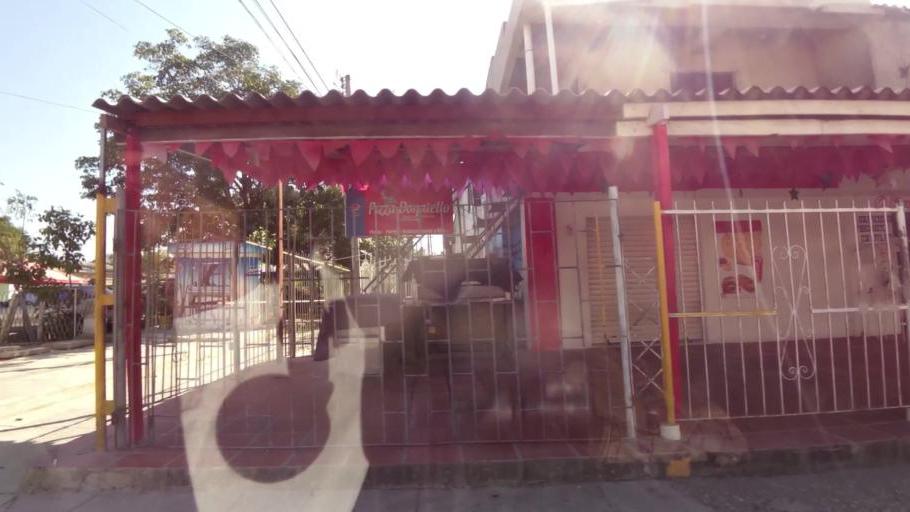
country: CO
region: Bolivar
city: Cartagena
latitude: 10.3949
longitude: -75.5151
